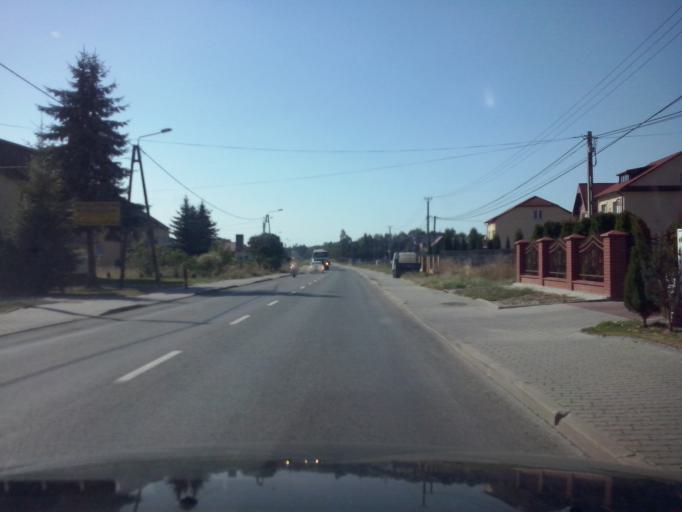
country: PL
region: Swietokrzyskie
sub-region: Powiat kielecki
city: Daleszyce
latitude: 50.8065
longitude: 20.7951
